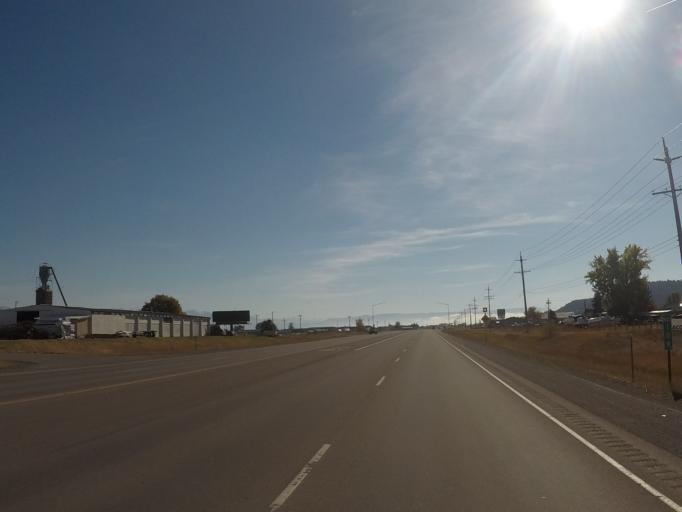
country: US
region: Montana
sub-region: Flathead County
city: Kalispell
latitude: 48.1409
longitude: -114.2807
